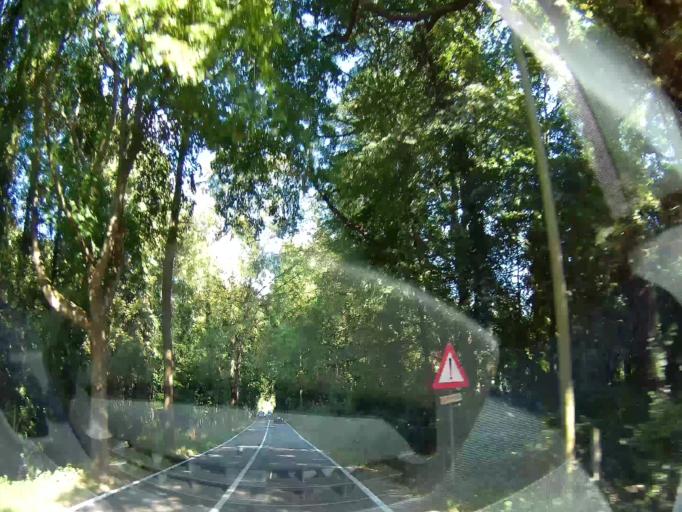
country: BE
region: Wallonia
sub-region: Province de Namur
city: Anhee
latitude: 50.3183
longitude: 4.8568
